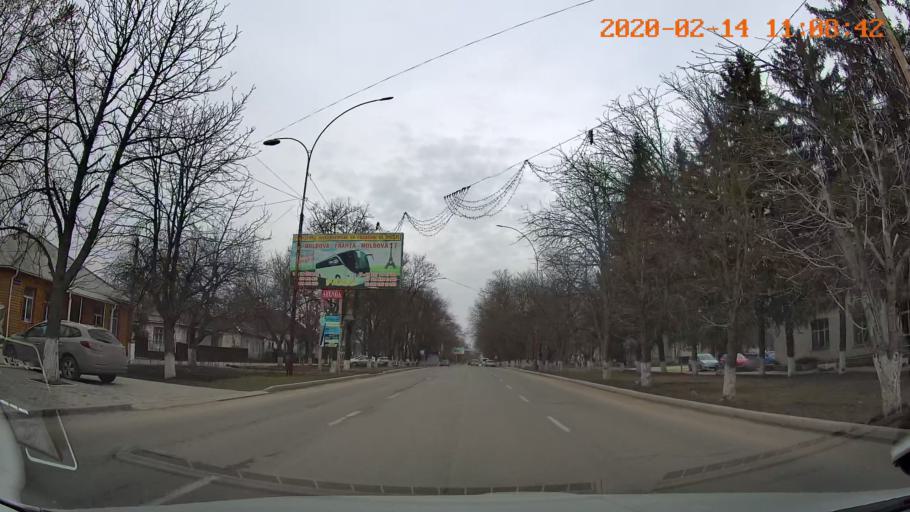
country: MD
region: Raionul Edinet
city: Edinet
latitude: 48.1735
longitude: 27.3000
